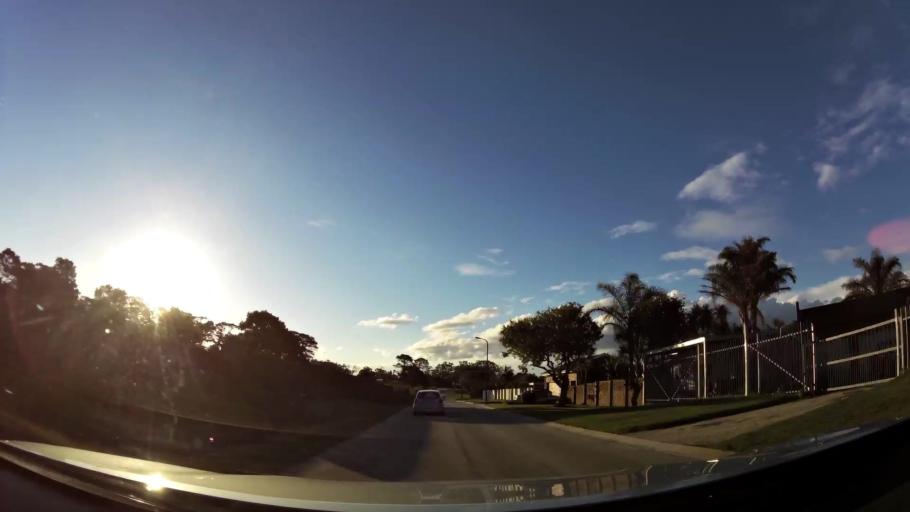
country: ZA
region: Eastern Cape
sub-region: Nelson Mandela Bay Metropolitan Municipality
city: Port Elizabeth
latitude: -33.9738
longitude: 25.4882
